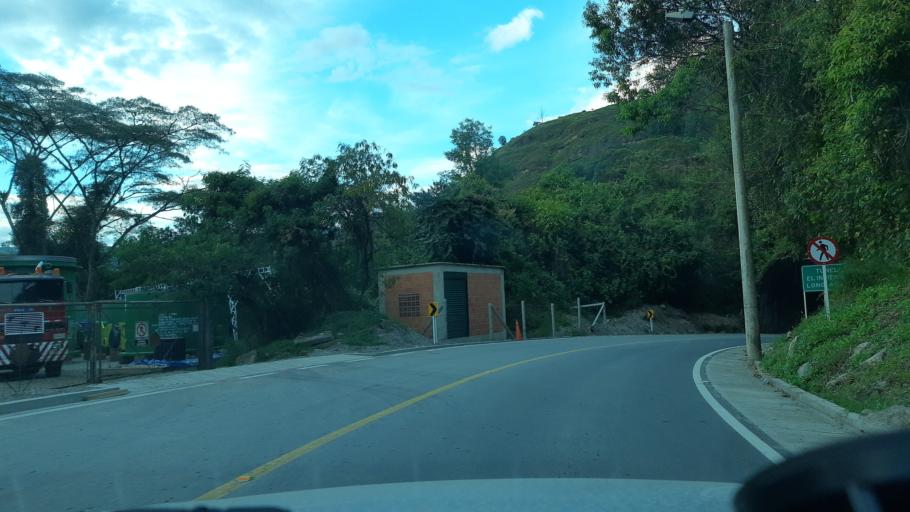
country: CO
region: Boyaca
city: Somondoco
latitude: 4.9968
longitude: -73.3525
